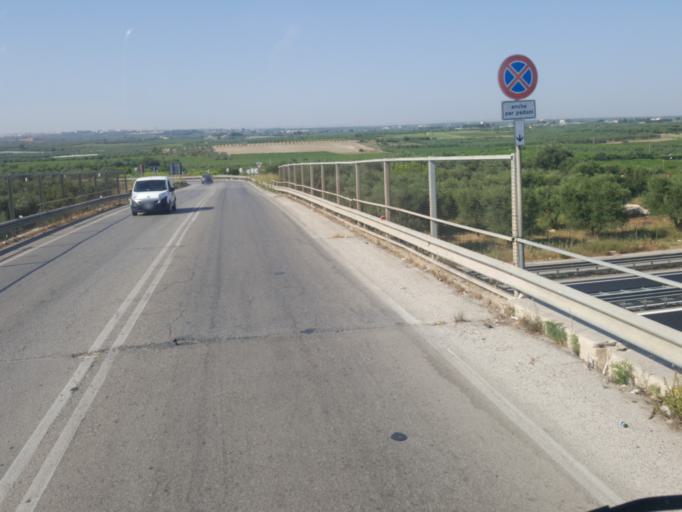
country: IT
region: Apulia
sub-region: Provincia di Barletta - Andria - Trani
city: Barletta
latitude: 41.3031
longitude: 16.3097
